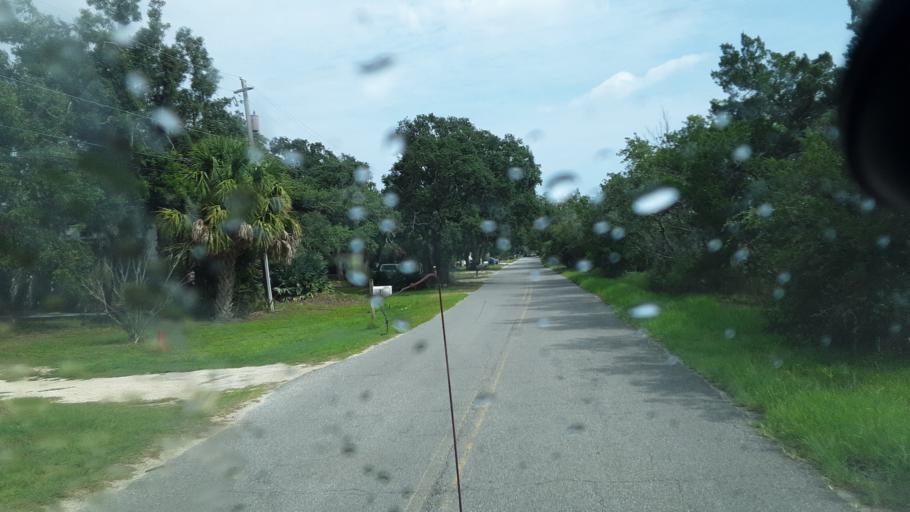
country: US
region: Georgia
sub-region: Chatham County
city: Tybee Island
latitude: 32.0146
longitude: -80.8688
